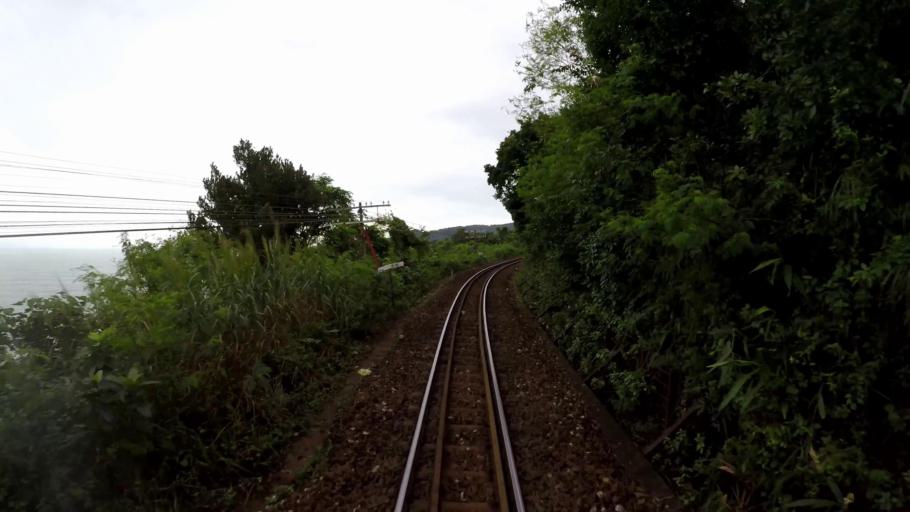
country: VN
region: Da Nang
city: Lien Chieu
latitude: 16.2150
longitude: 108.1249
